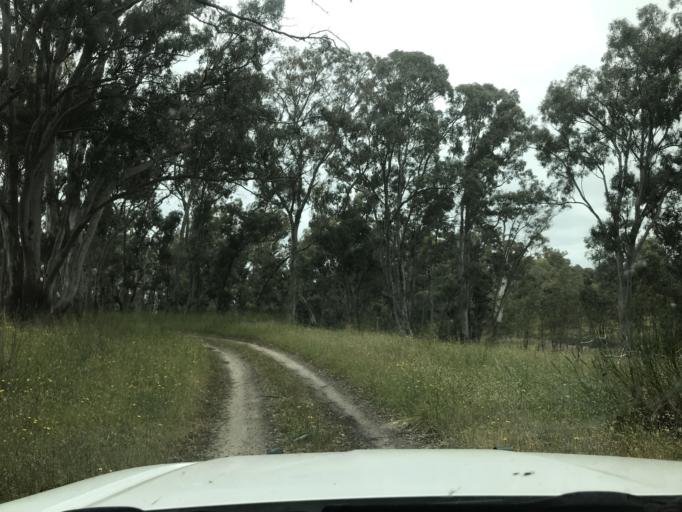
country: AU
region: South Australia
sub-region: Wattle Range
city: Penola
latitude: -37.1922
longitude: 140.9713
